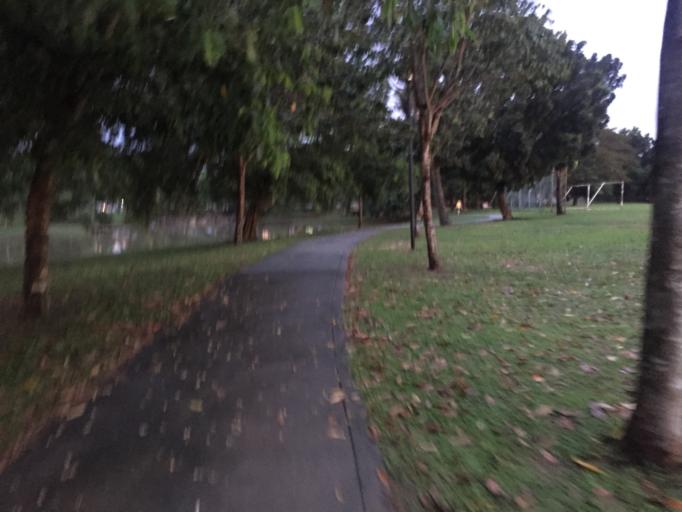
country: MY
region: Selangor
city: Klang
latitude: 2.9881
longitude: 101.4367
